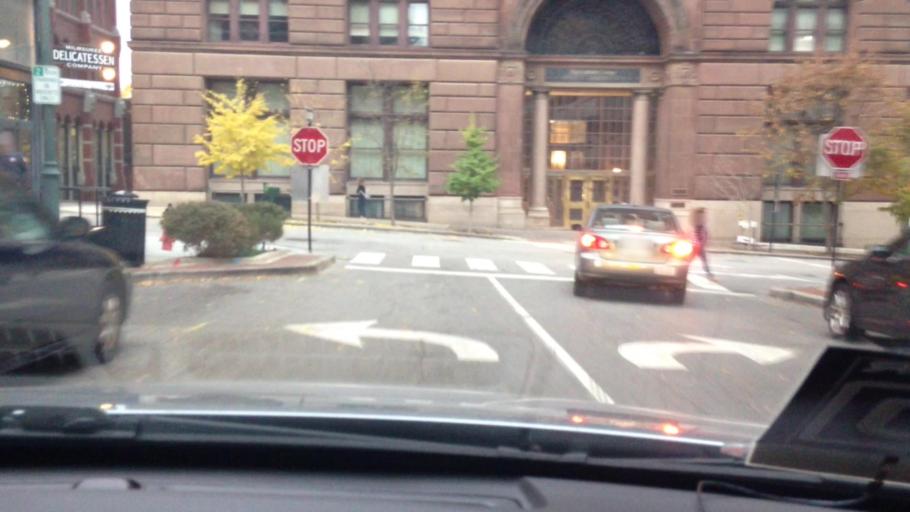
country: US
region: Missouri
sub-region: Jackson County
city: Kansas City
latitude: 39.1033
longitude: -94.5840
